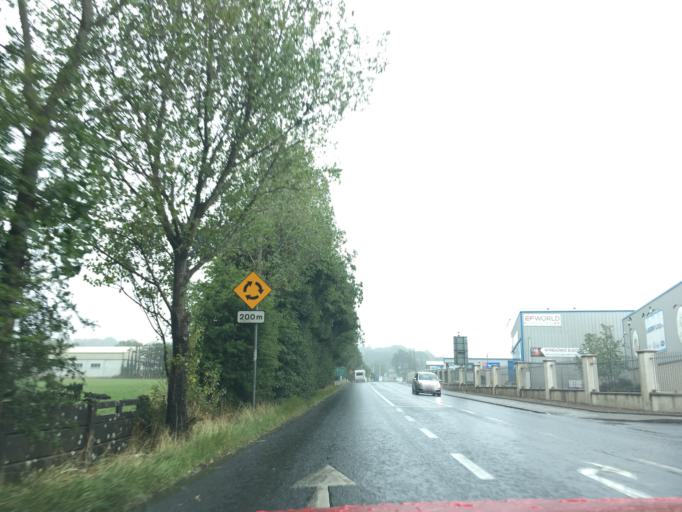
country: IE
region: Leinster
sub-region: Loch Garman
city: New Ross
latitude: 52.3883
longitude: -6.9279
